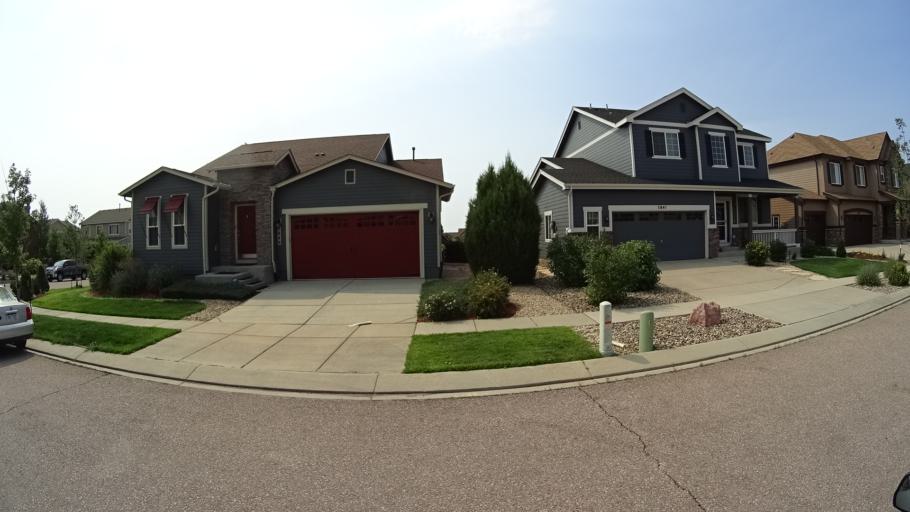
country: US
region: Colorado
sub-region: El Paso County
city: Black Forest
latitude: 38.9622
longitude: -104.7191
